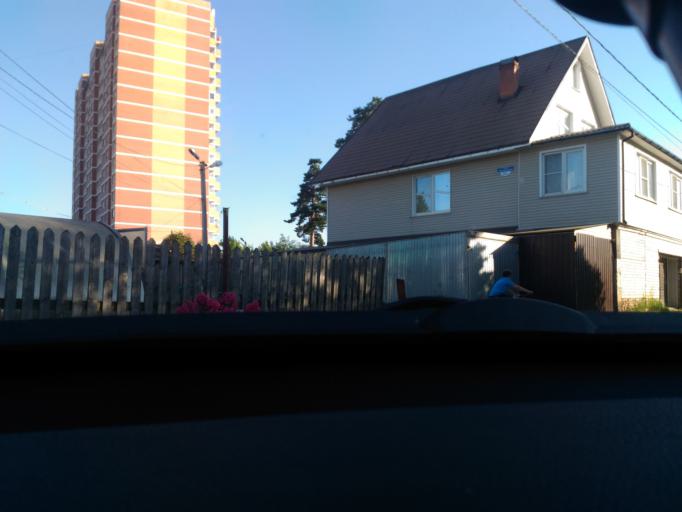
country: RU
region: Moskovskaya
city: Povarovo
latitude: 56.0818
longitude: 37.0625
